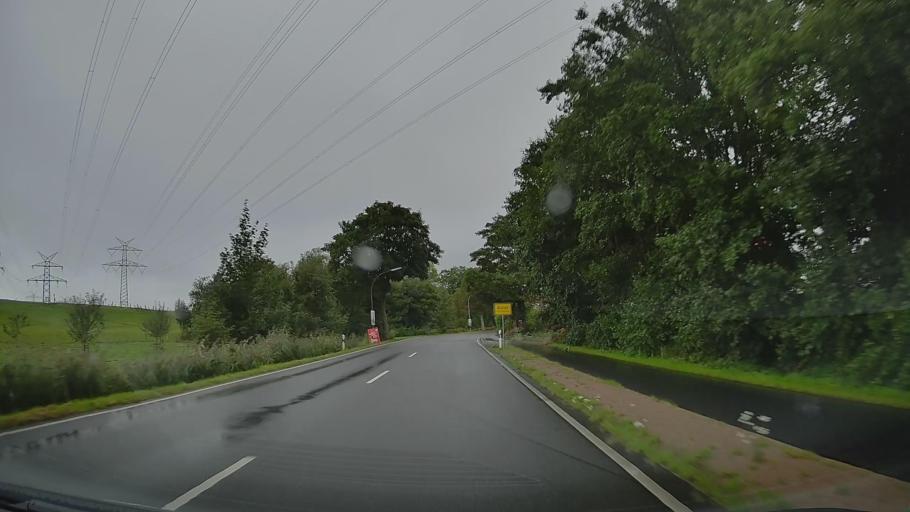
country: DE
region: Schleswig-Holstein
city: Buttel
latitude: 53.8964
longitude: 9.2363
